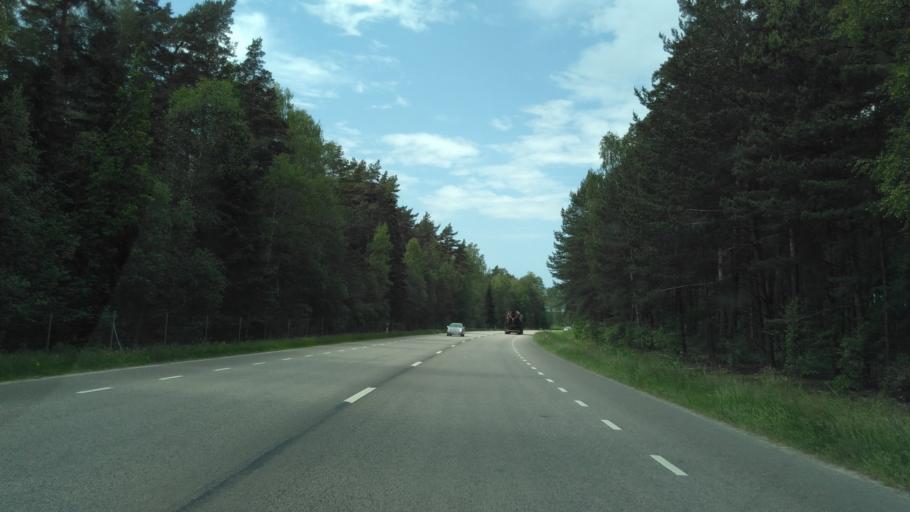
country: SE
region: Vaestra Goetaland
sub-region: Lidkopings Kommun
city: Lidkoping
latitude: 58.4871
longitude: 13.1605
